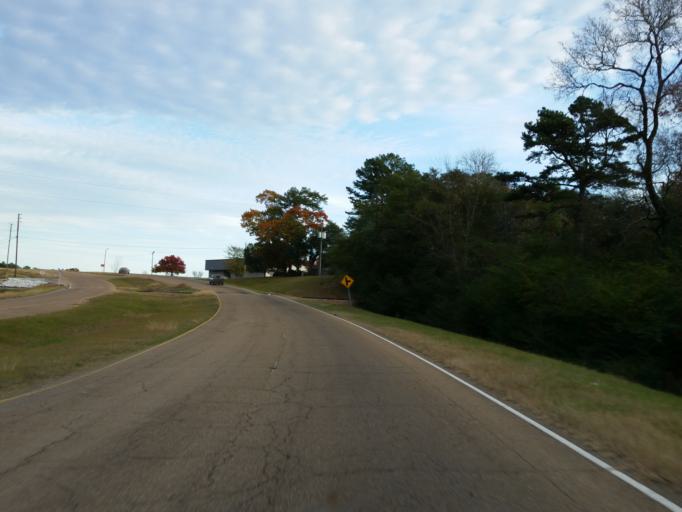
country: US
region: Mississippi
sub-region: Lauderdale County
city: Marion
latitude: 32.4113
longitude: -88.6299
